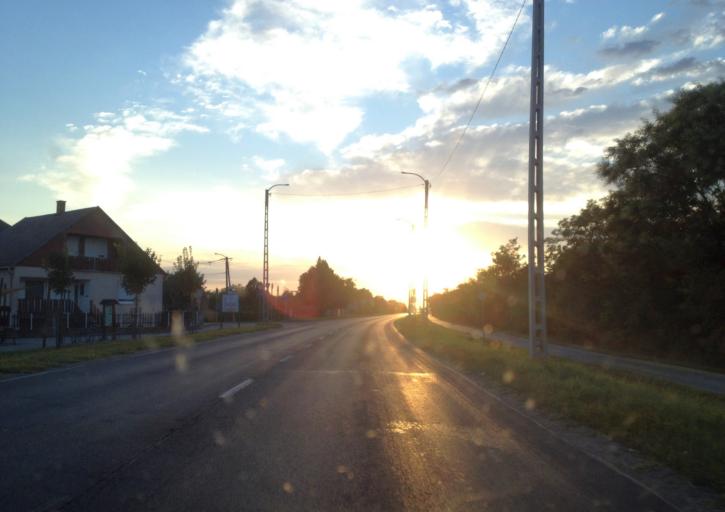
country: HU
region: Gyor-Moson-Sopron
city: Mosonmagyarovar
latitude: 47.8973
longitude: 17.2091
